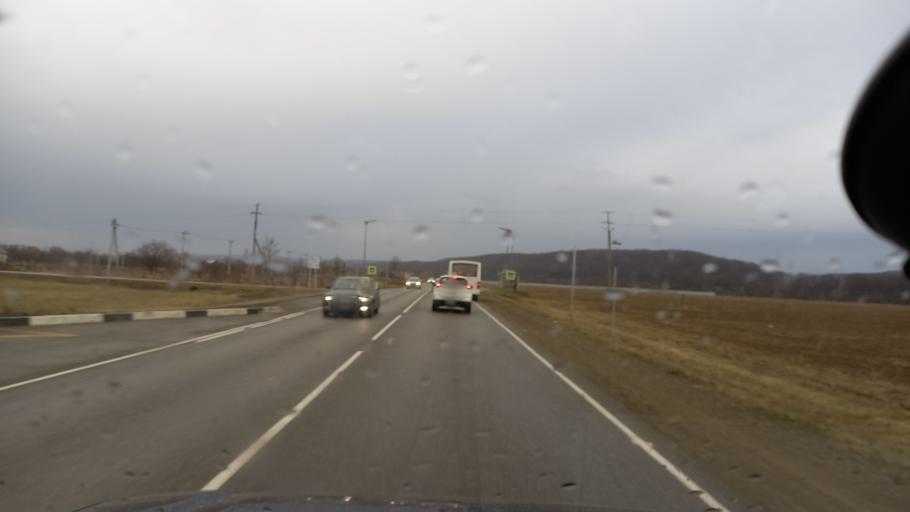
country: RU
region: Adygeya
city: Tul'skiy
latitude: 44.5324
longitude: 40.1383
